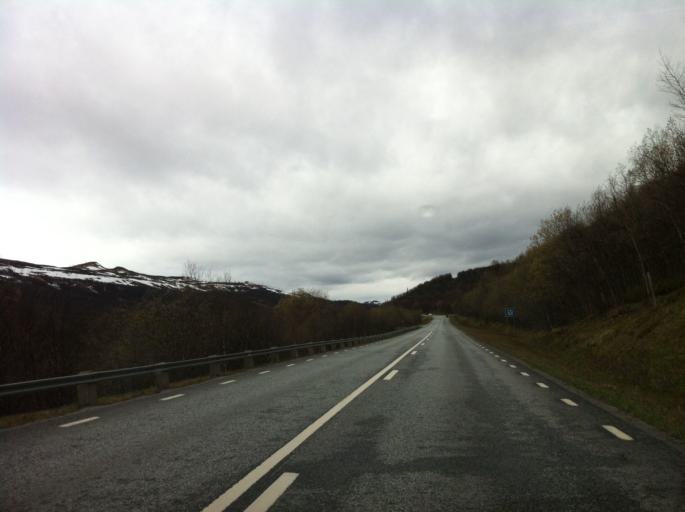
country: NO
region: Sor-Trondelag
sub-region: Tydal
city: Aas
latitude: 62.5520
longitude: 12.2918
